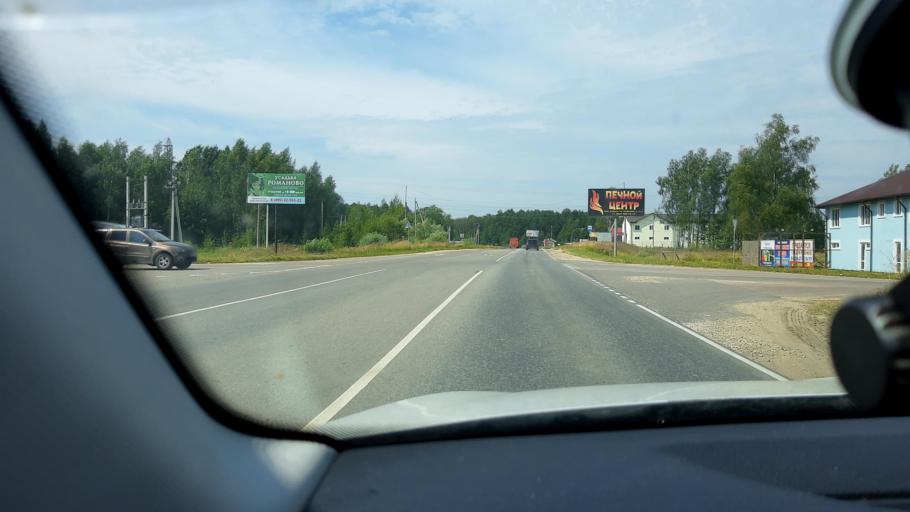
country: RU
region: Tula
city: Zaokskiy
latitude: 54.7463
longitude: 37.4089
